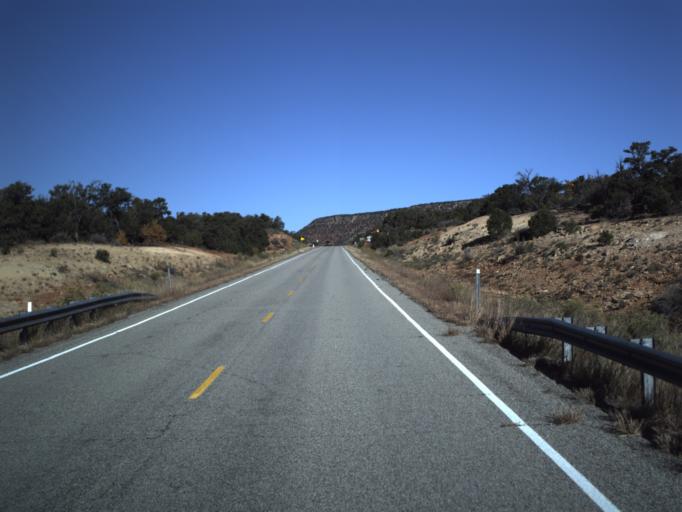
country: US
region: Utah
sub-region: San Juan County
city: Blanding
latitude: 37.5759
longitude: -109.8812
